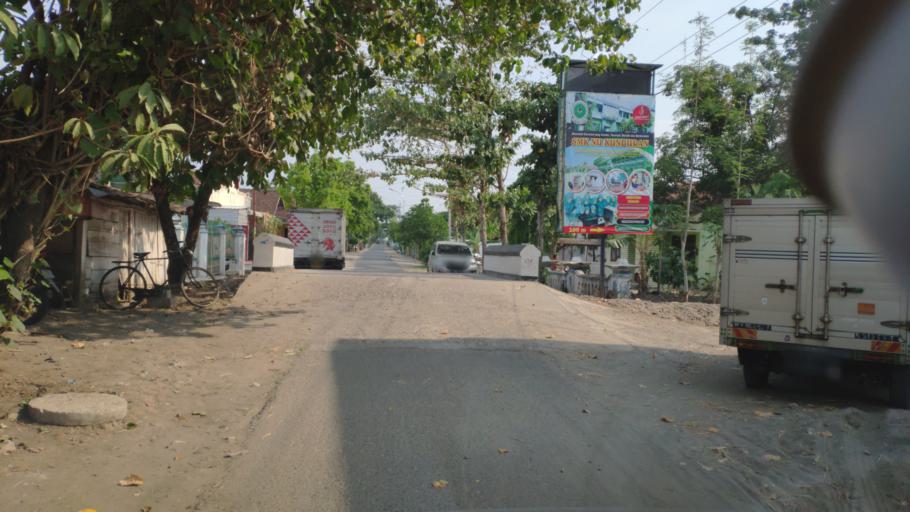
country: ID
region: Central Java
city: Jagong
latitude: -7.0518
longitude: 111.2393
